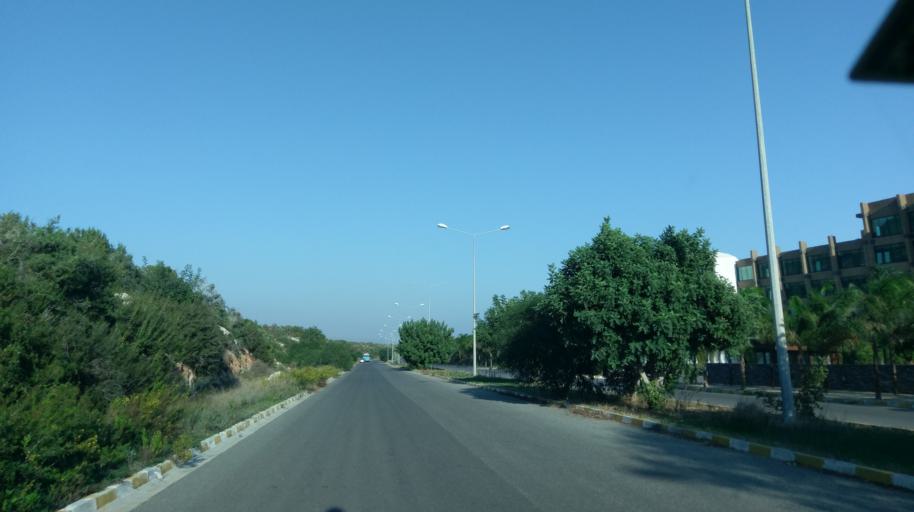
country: CY
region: Ammochostos
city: Leonarisso
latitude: 35.3795
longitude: 34.0877
